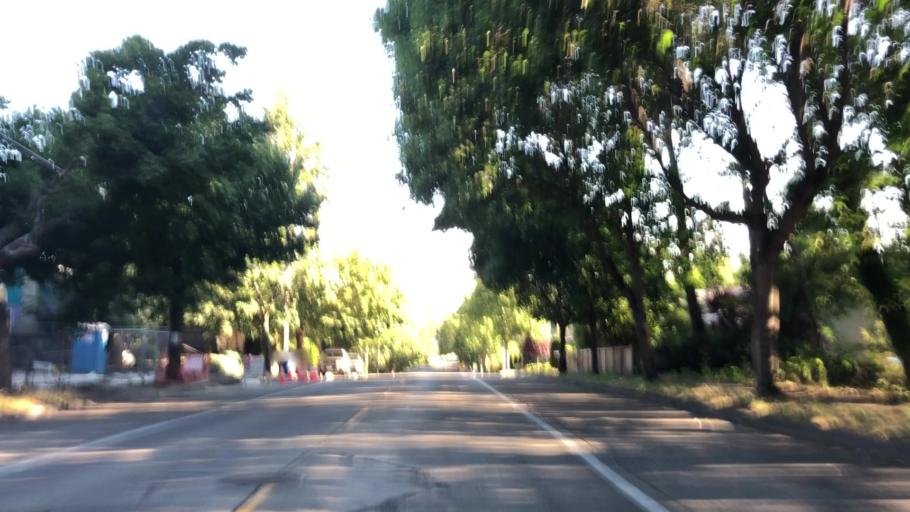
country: US
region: Washington
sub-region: King County
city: White Center
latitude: 47.5364
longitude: -122.3551
